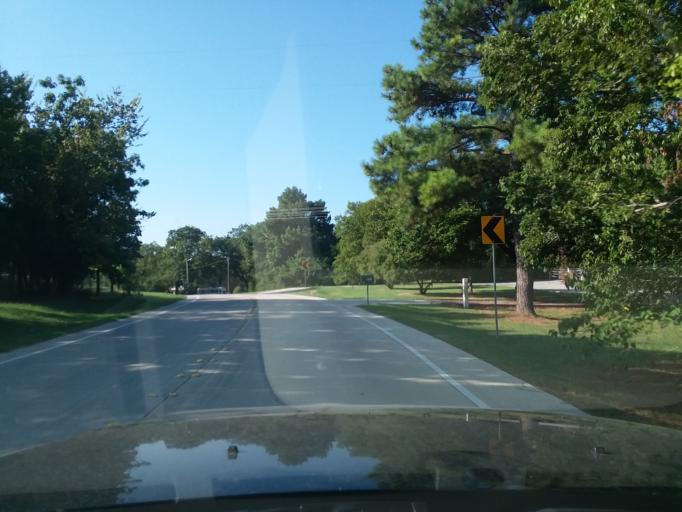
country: US
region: Texas
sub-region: Denton County
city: Copper Canyon
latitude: 33.0970
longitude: -97.0882
